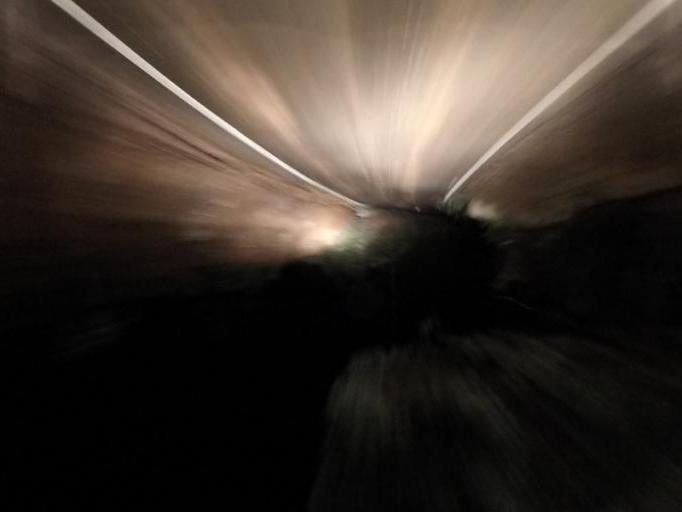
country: IN
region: Tamil Nadu
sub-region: Nilgiri
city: Kotagiri
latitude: 11.4648
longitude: 76.8206
